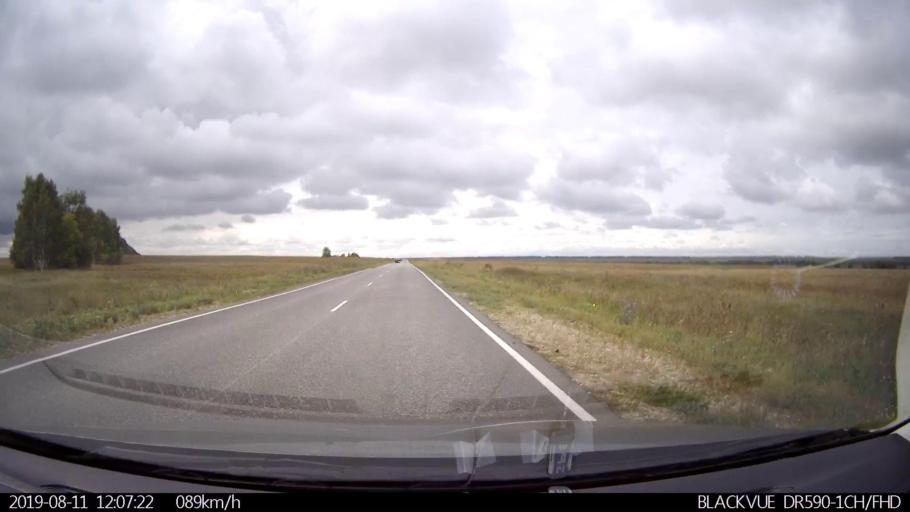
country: RU
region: Ulyanovsk
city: Silikatnyy
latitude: 53.9967
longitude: 48.0962
